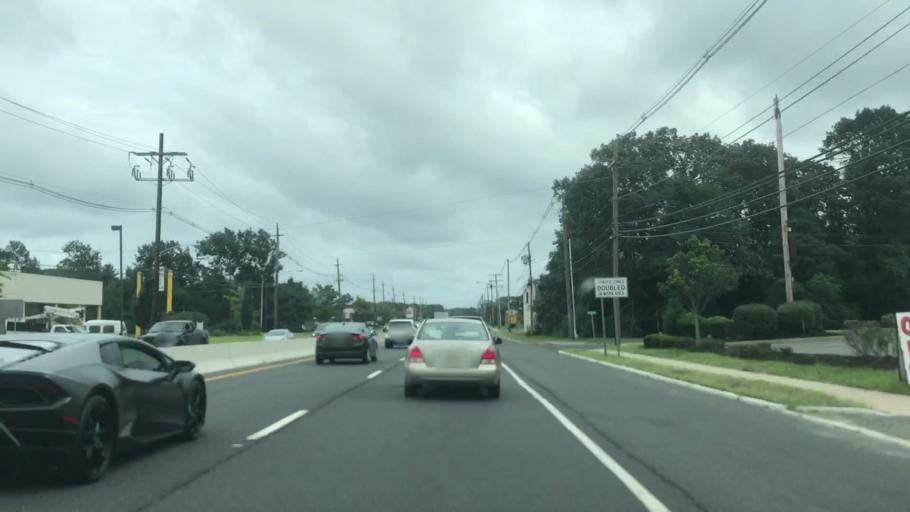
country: US
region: New Jersey
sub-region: Monmouth County
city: Eatontown
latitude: 40.2841
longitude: -74.0498
